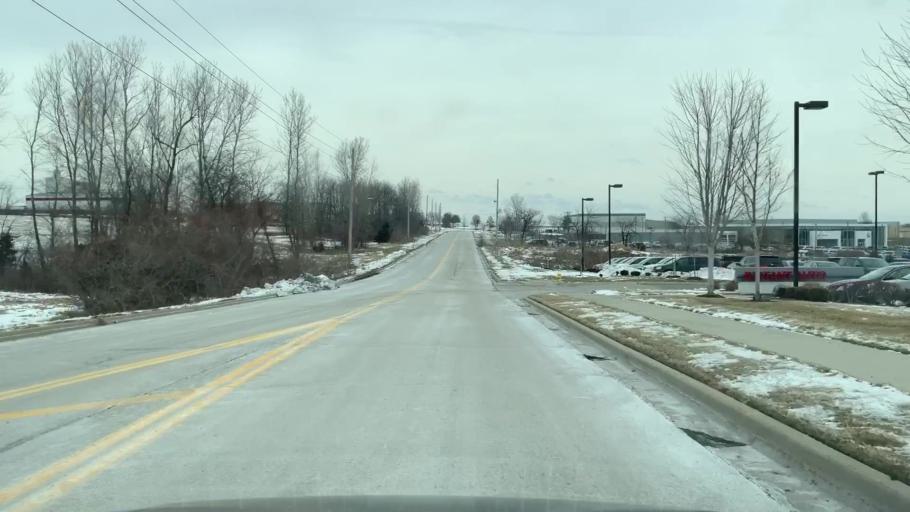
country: US
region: Missouri
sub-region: Jackson County
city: Lees Summit
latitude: 38.9504
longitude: -94.3640
